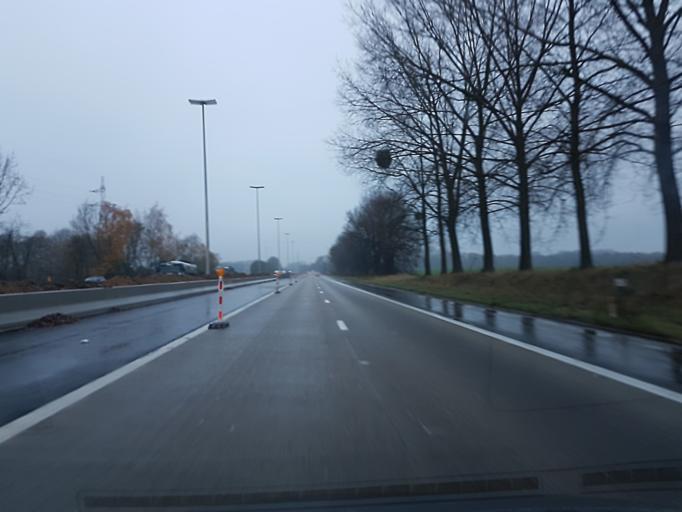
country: BE
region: Wallonia
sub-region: Province de Namur
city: Noville-les-Bois
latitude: 50.5301
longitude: 4.9706
